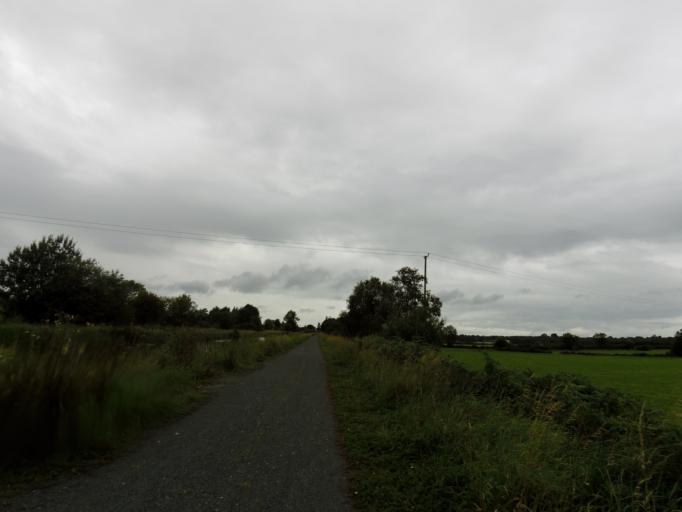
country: IE
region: Leinster
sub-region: An Iarmhi
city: Moate
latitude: 53.5884
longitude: -7.6361
